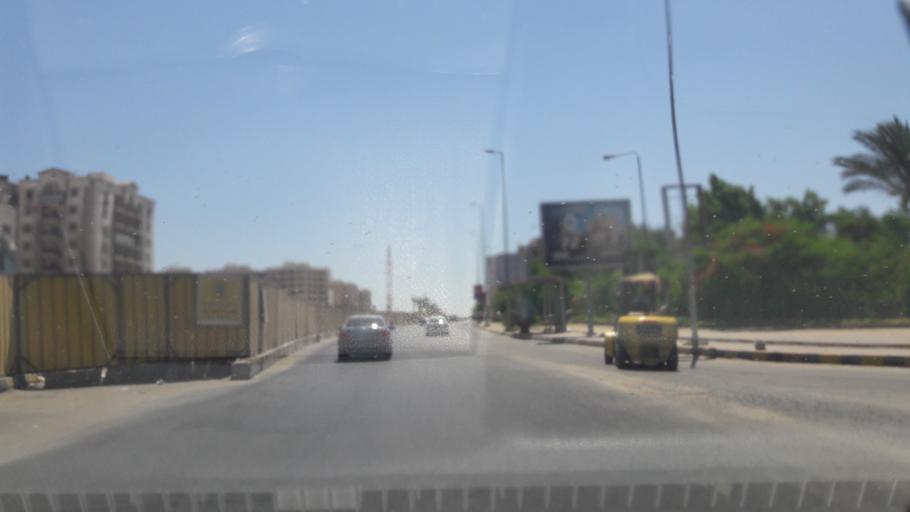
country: EG
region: Al Jizah
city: Madinat Sittah Uktubar
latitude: 29.9752
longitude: 30.9422
